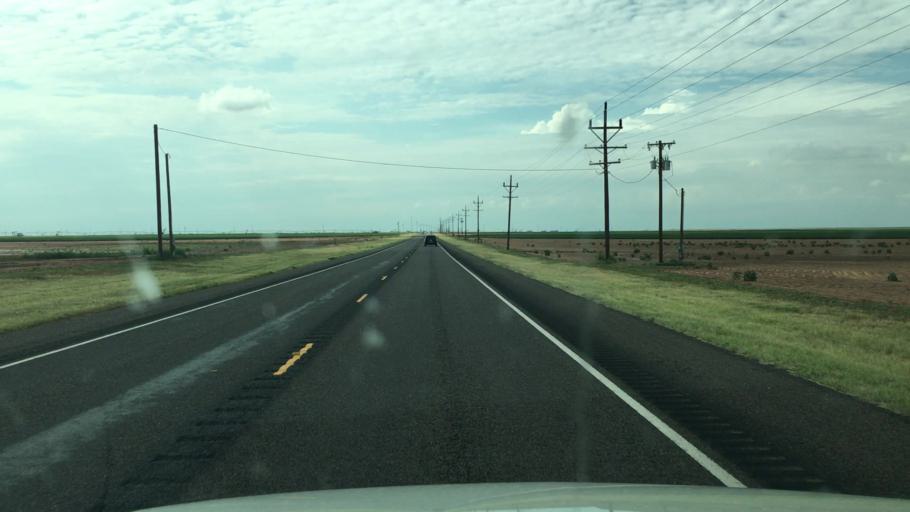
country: US
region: Texas
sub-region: Dawson County
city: Lamesa
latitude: 32.8830
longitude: -102.0828
